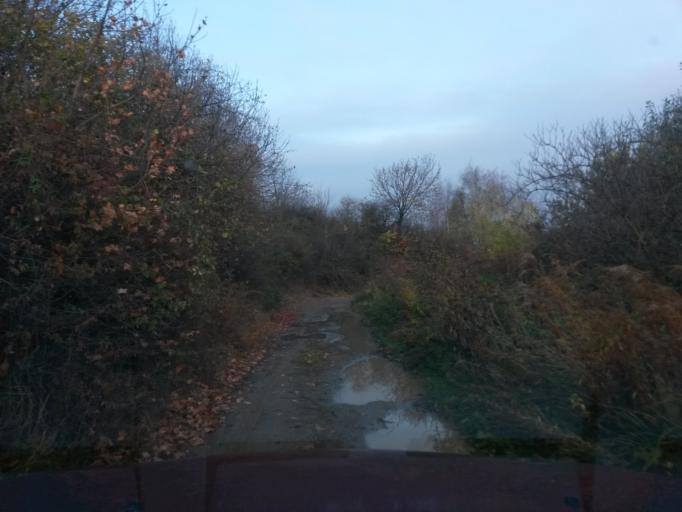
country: SK
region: Kosicky
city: Kosice
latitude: 48.7674
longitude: 21.2001
